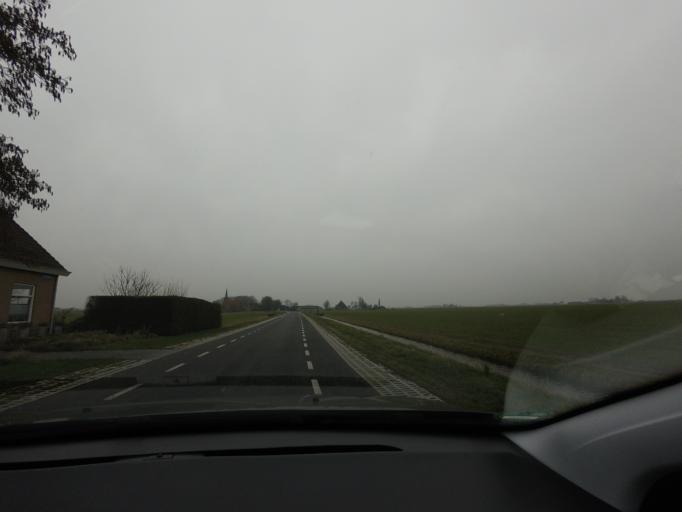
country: NL
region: Friesland
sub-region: Sudwest Fryslan
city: Bolsward
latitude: 53.1066
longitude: 5.5418
